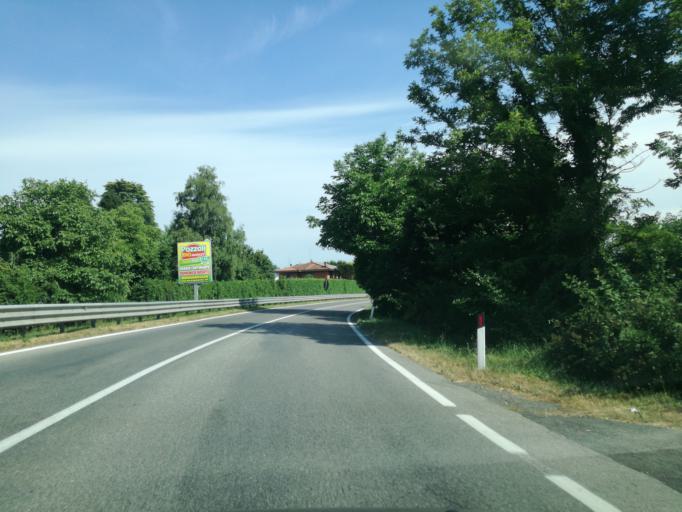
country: IT
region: Lombardy
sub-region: Provincia di Monza e Brianza
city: Bernareggio
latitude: 45.6493
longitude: 9.3981
